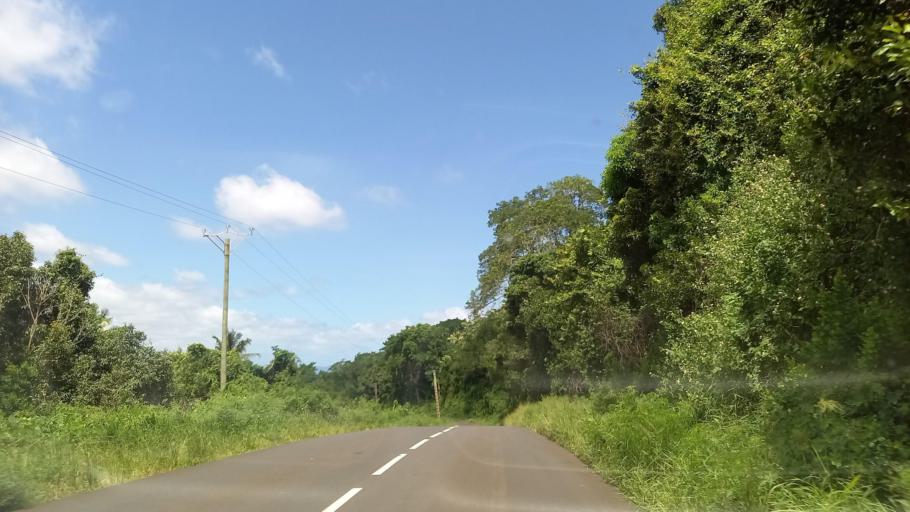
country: YT
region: Acoua
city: Acoua
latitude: -12.7432
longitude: 45.0544
